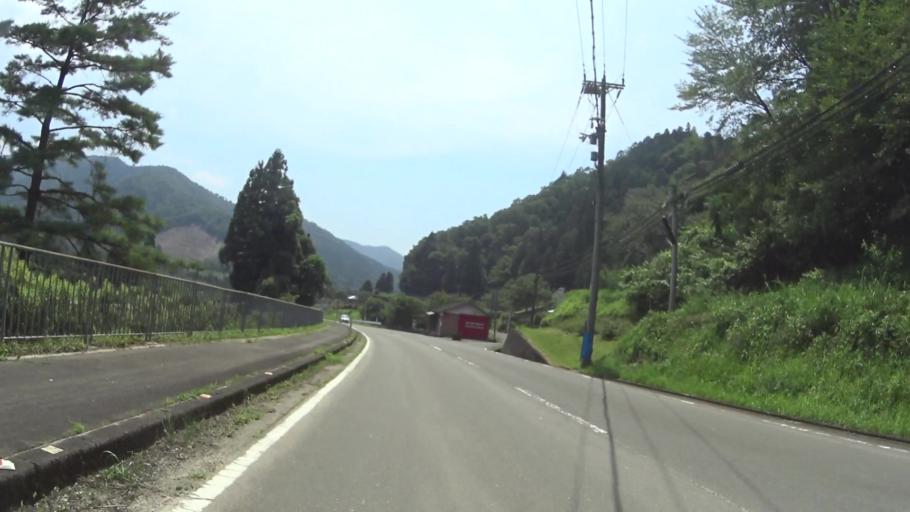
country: JP
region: Kyoto
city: Ayabe
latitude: 35.2688
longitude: 135.4304
